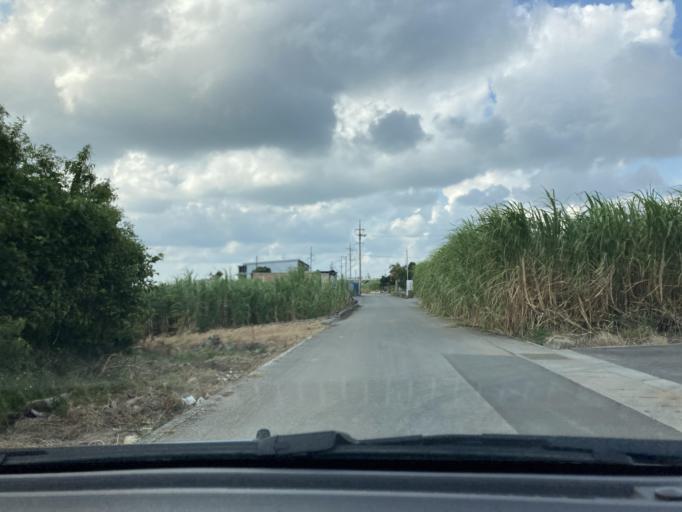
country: JP
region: Okinawa
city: Itoman
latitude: 26.0845
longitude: 127.6630
